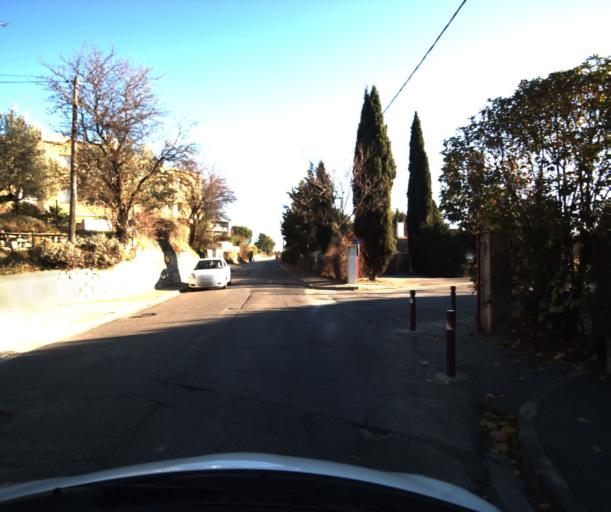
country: FR
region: Provence-Alpes-Cote d'Azur
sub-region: Departement du Vaucluse
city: Pertuis
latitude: 43.6888
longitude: 5.5085
